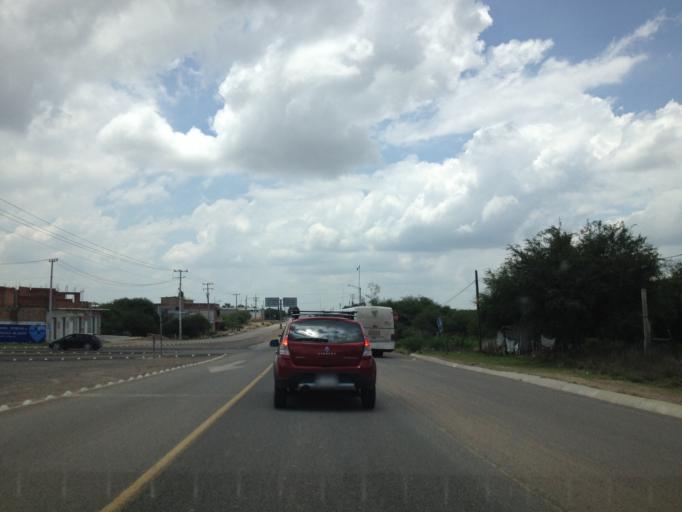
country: MX
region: Guanajuato
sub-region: Dolores Hidalgo Cuna de la Independencia Nacional
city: Colonia Padre Hidalgo
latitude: 21.1586
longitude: -100.9636
